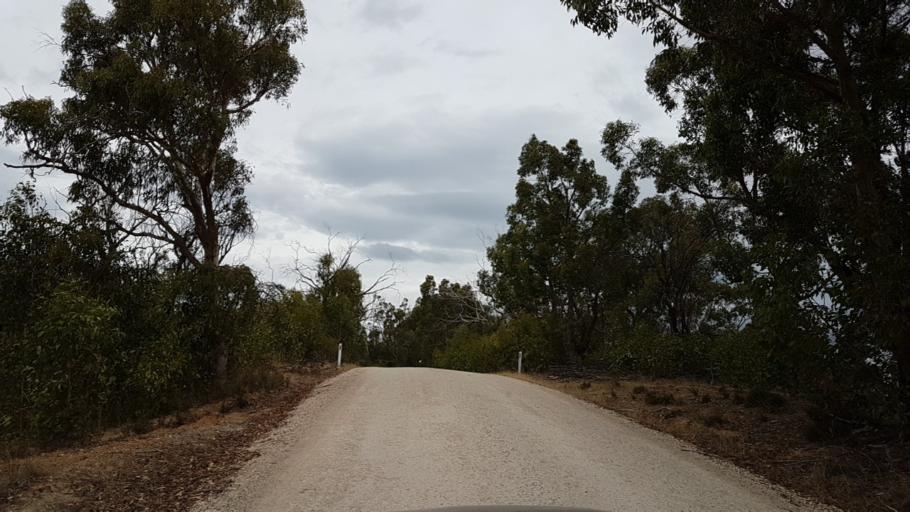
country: AU
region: South Australia
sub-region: Tea Tree Gully
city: Golden Grove
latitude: -34.7756
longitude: 138.8138
